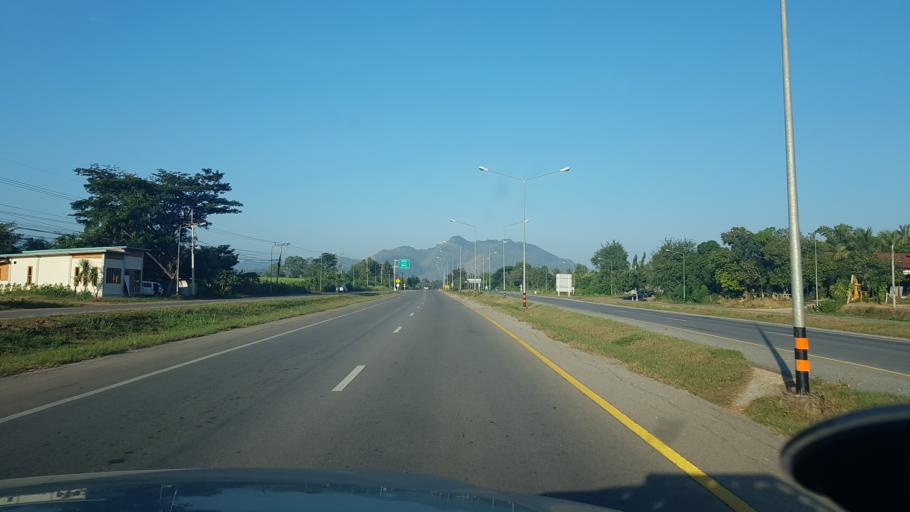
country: TH
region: Chaiyaphum
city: Khon San
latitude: 16.5956
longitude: 101.9234
